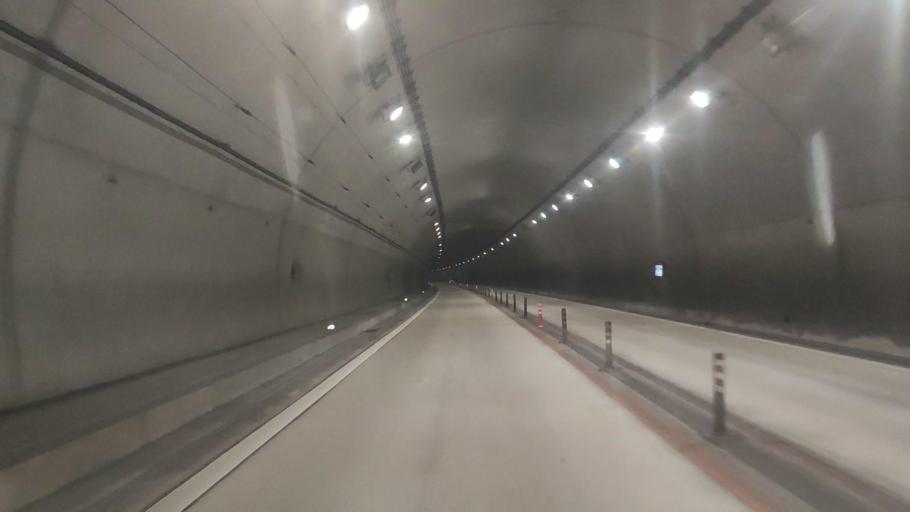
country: JP
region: Nagasaki
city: Shimabara
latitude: 32.7779
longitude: 130.3559
